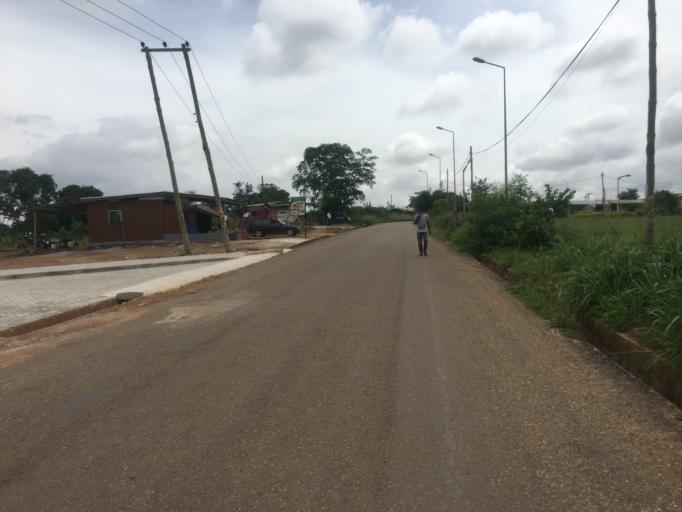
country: GH
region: Ashanti
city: Mamponteng
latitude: 6.6876
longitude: -1.5569
